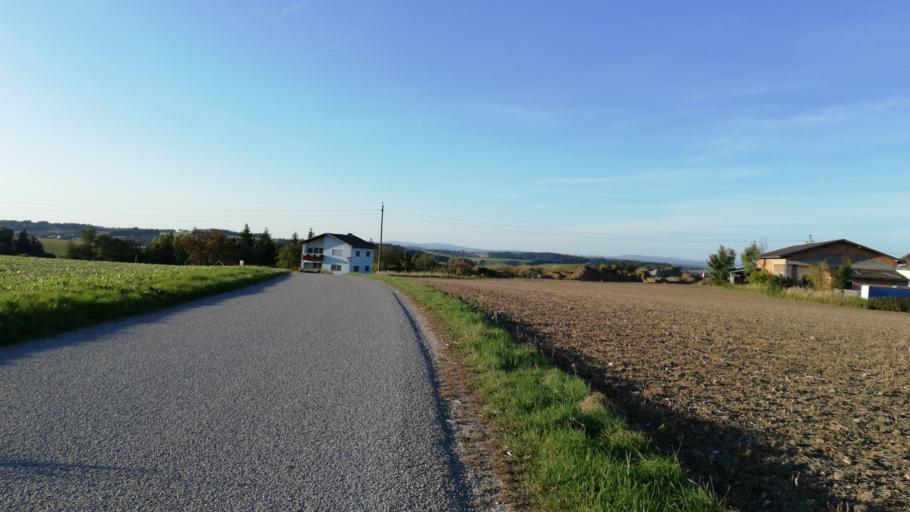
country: AT
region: Upper Austria
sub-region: Wels-Land
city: Offenhausen
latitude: 48.1639
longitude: 13.8588
